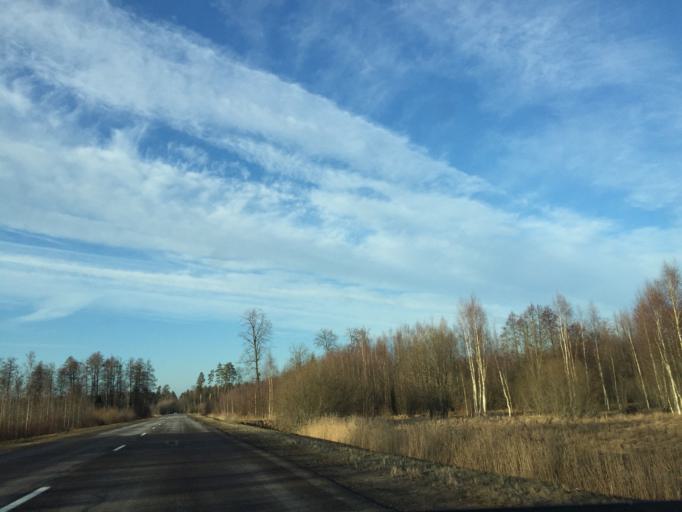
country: LV
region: Kekava
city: Balozi
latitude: 56.8174
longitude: 24.0627
